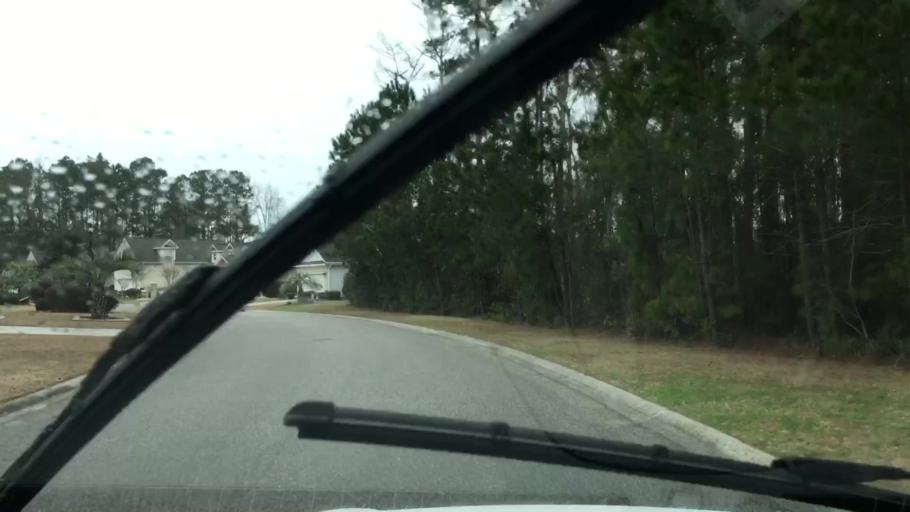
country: US
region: South Carolina
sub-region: Horry County
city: Red Hill
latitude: 33.7764
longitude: -79.0077
